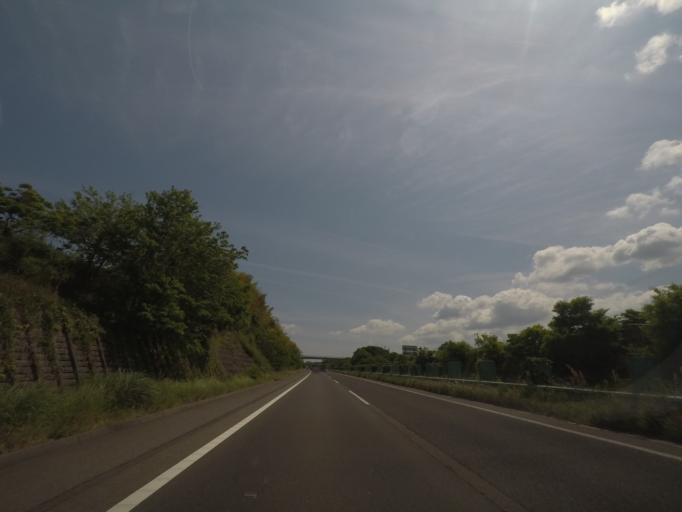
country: JP
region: Hyogo
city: Sumoto
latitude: 34.4348
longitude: 134.8706
